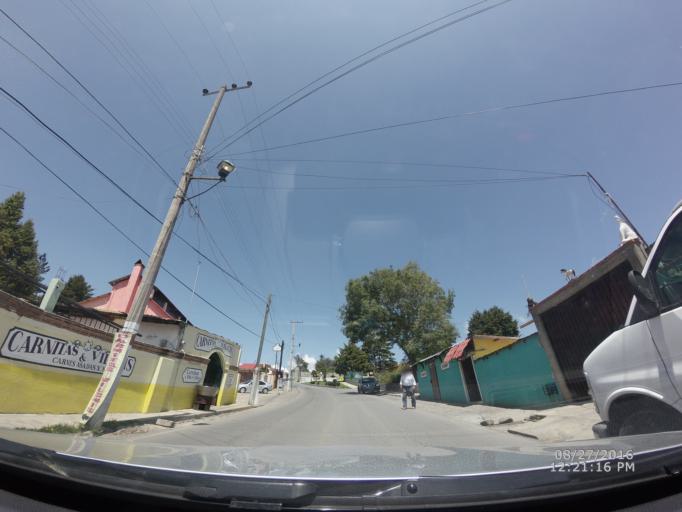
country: MX
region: Hidalgo
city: Mineral del Monte
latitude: 20.1358
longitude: -98.6769
